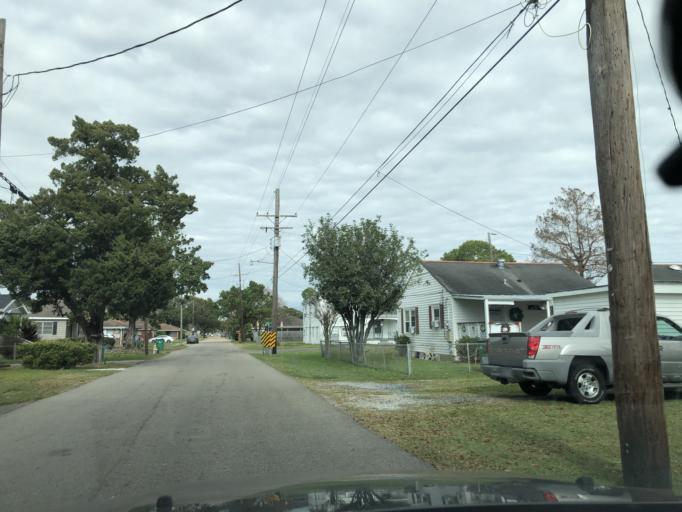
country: US
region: Louisiana
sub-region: Jefferson Parish
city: Metairie Terrace
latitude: 29.9834
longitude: -90.1615
